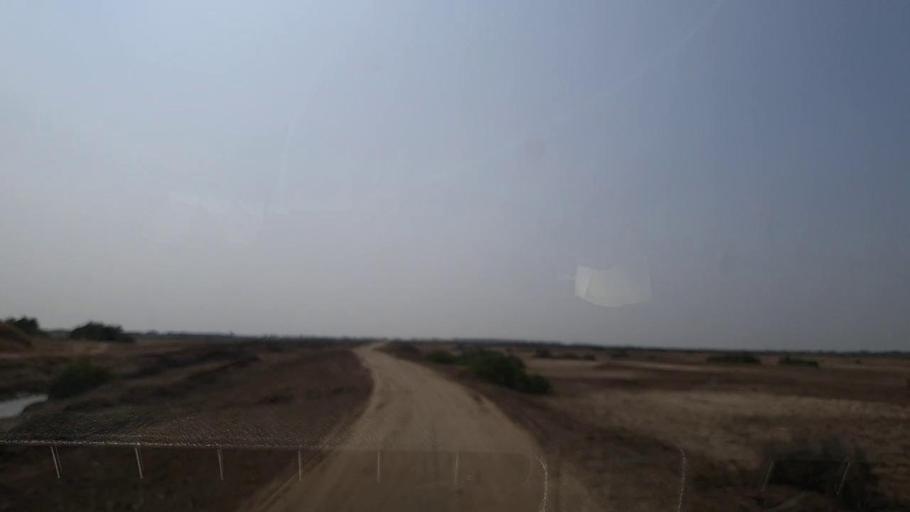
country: PK
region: Sindh
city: Mirpur Sakro
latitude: 24.5394
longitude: 67.7852
